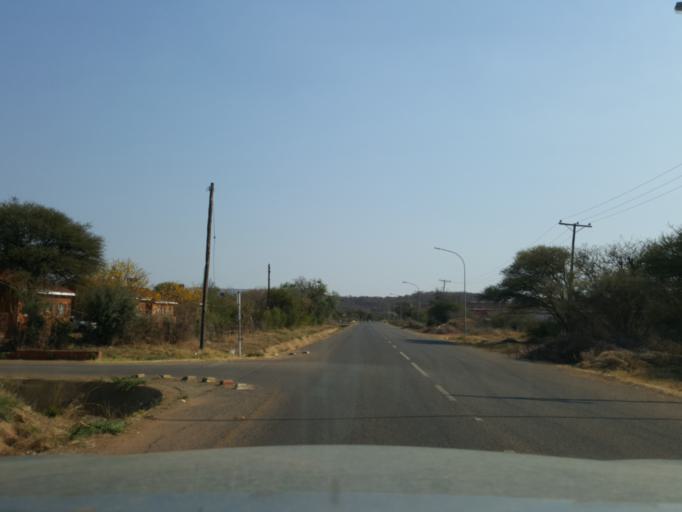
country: BW
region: South East
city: Lobatse
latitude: -25.1902
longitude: 25.6947
